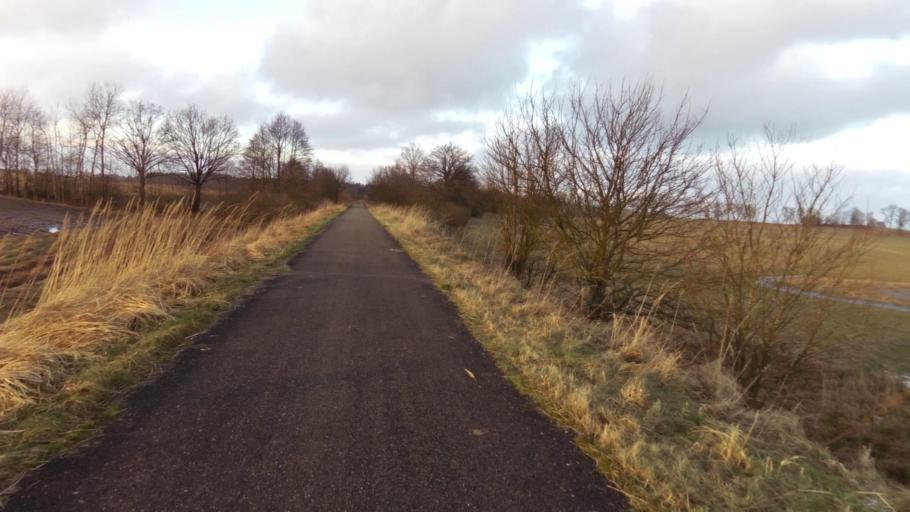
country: PL
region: West Pomeranian Voivodeship
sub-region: Powiat drawski
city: Zlocieniec
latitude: 53.6274
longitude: 16.0566
